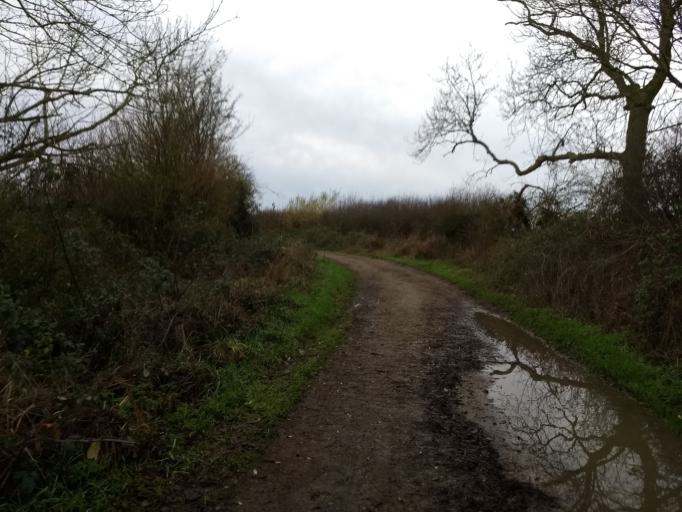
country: GB
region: England
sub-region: Buckinghamshire
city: Newton Longville
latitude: 51.9849
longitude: -0.7870
